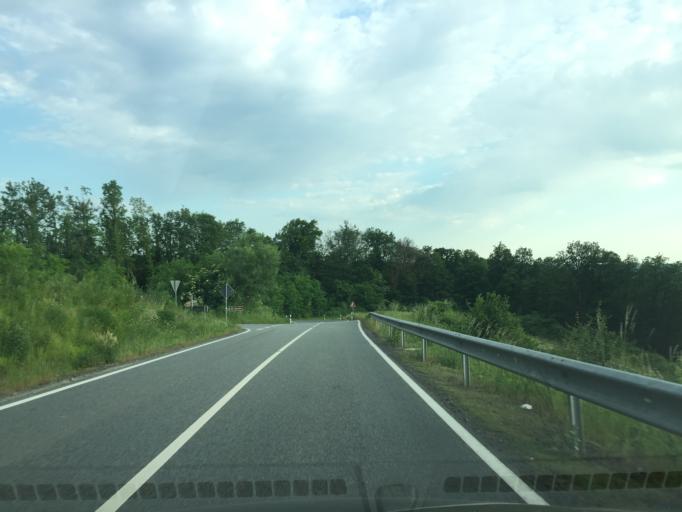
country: DE
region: Rheinland-Pfalz
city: Bendorf
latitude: 50.4424
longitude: 7.5840
